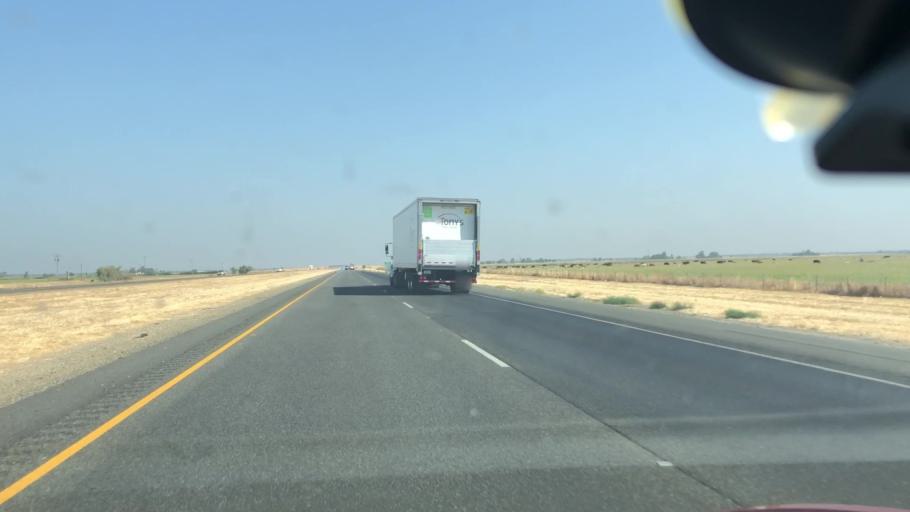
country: US
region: California
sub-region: Sacramento County
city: Laguna
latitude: 38.3545
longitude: -121.4723
